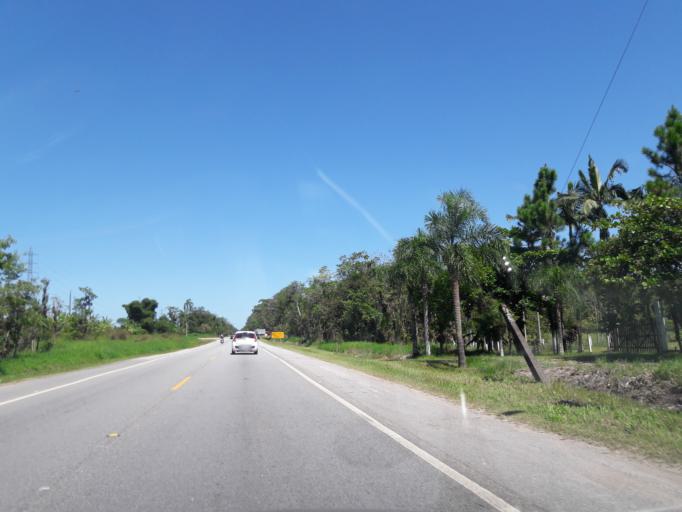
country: BR
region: Parana
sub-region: Pontal Do Parana
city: Pontal do Parana
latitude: -25.6406
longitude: -48.5334
